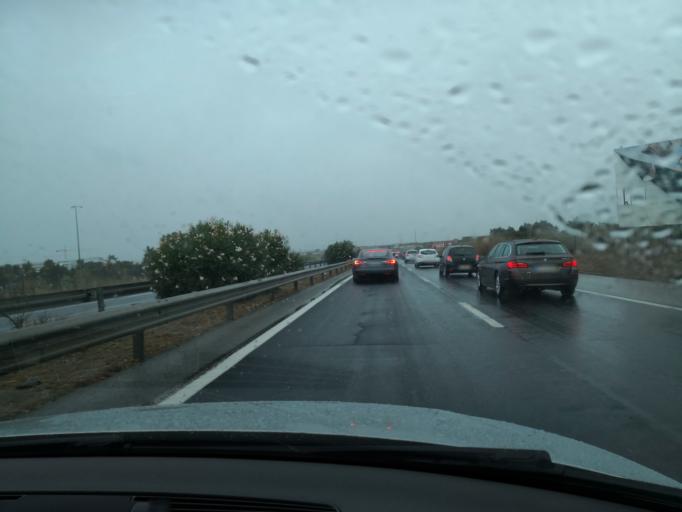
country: PT
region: Setubal
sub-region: Montijo
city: Montijo
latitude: 38.6957
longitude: -8.9394
